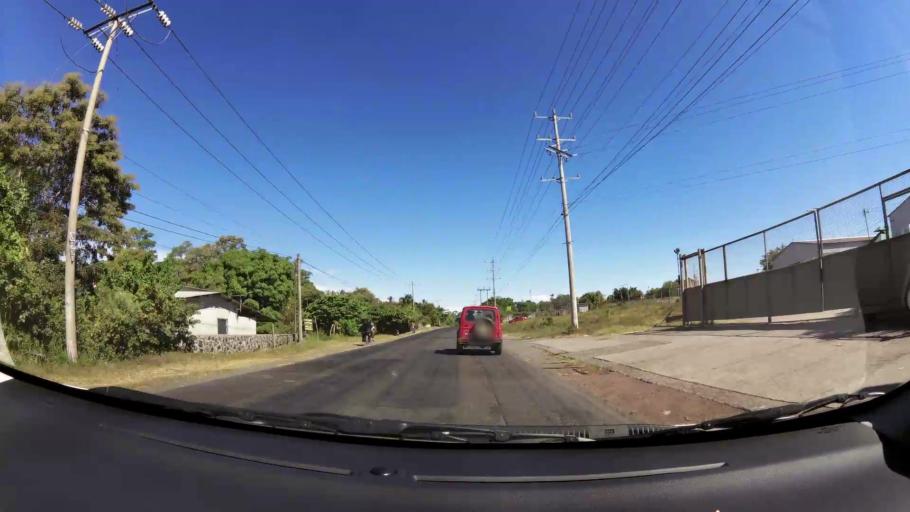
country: SV
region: La Libertad
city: San Juan Opico
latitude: 13.8047
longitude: -89.3588
